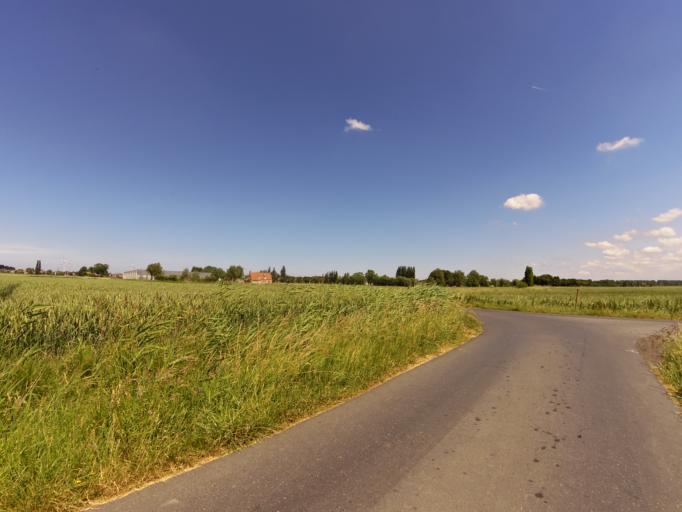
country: BE
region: Flanders
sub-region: Provincie West-Vlaanderen
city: Gistel
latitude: 51.1471
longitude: 2.9803
